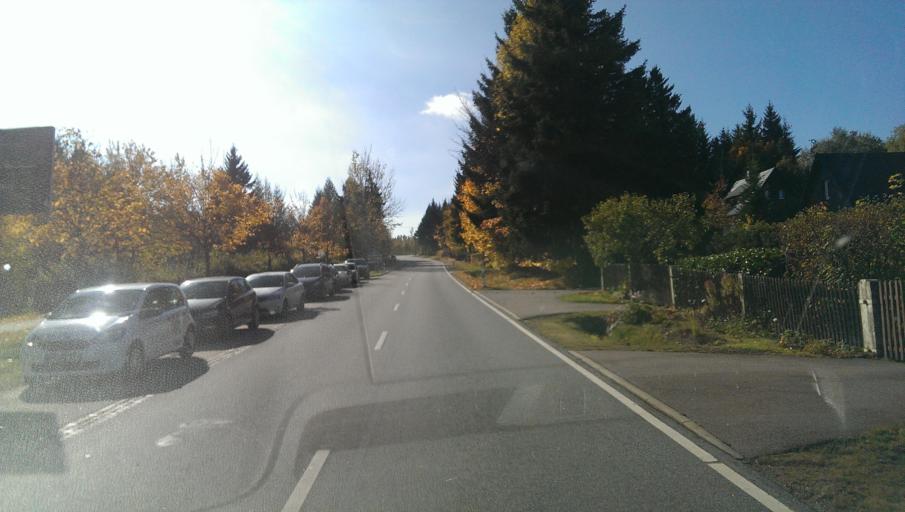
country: DE
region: Saxony
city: Altenberg
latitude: 50.7634
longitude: 13.7517
